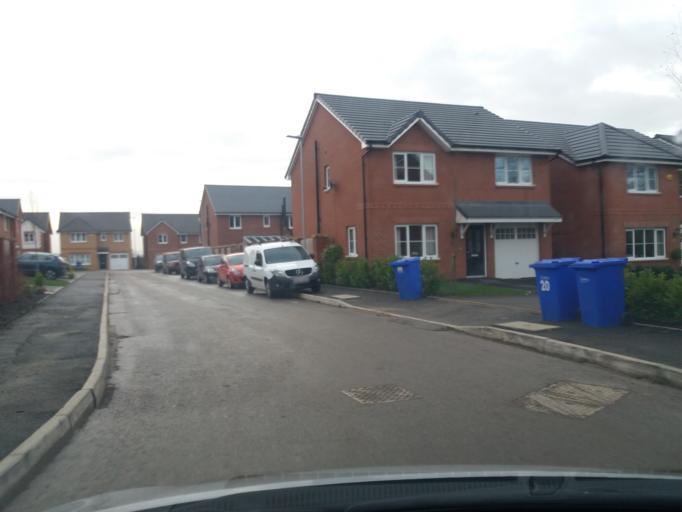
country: GB
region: England
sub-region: Lancashire
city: Adlington
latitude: 53.6145
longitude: -2.5949
